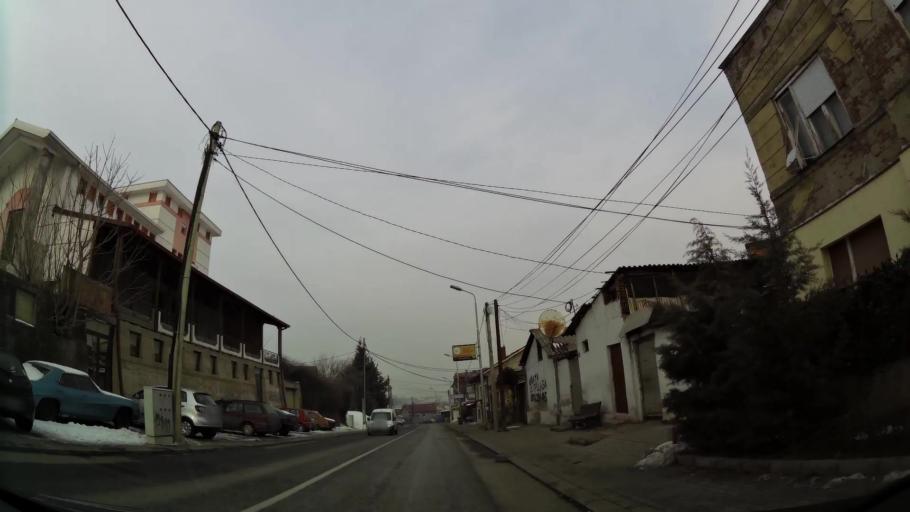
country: MK
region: Karpos
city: Skopje
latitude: 42.0053
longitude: 21.4335
